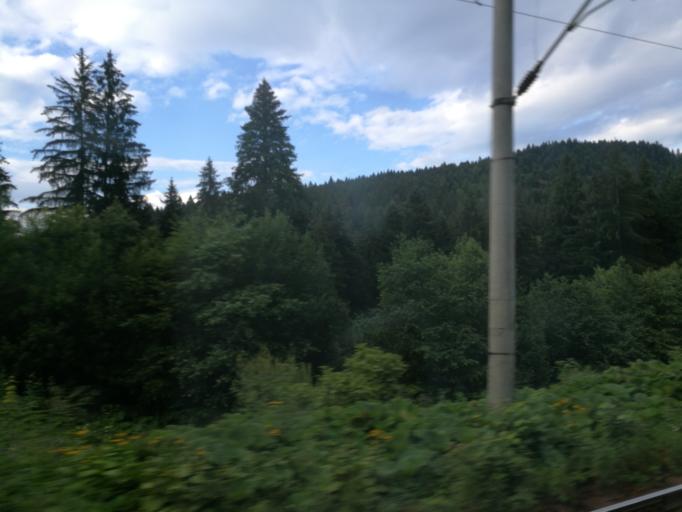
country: RO
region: Brasov
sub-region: Oras Predeal
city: Predeal
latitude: 45.5216
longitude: 25.5914
